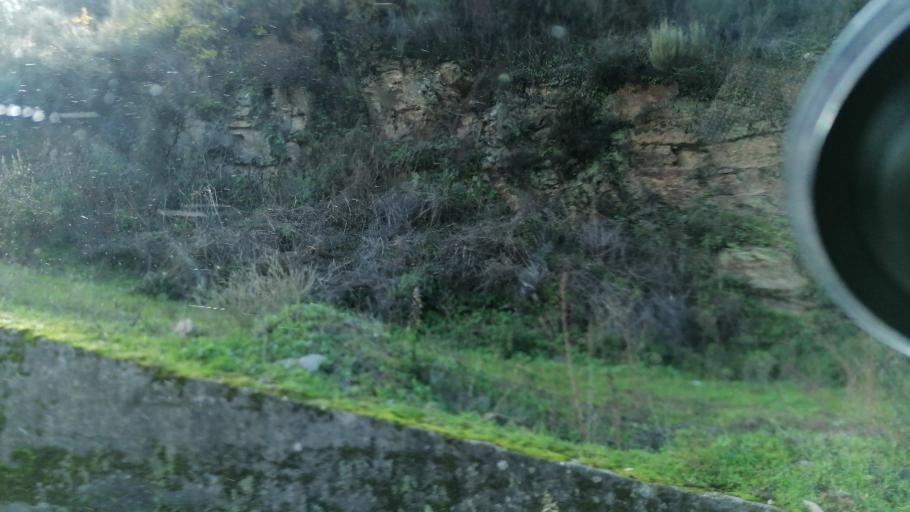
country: PT
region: Vila Real
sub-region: Peso da Regua
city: Peso da Regua
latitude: 41.1386
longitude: -7.7779
